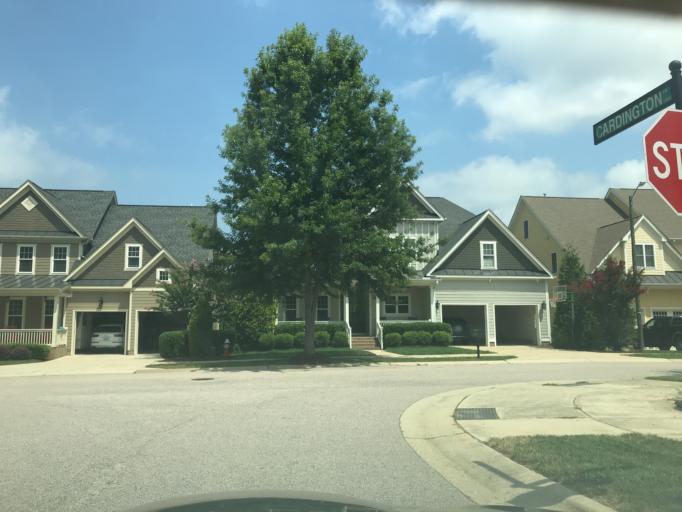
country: US
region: North Carolina
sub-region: Wake County
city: Wake Forest
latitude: 35.9304
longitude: -78.5697
